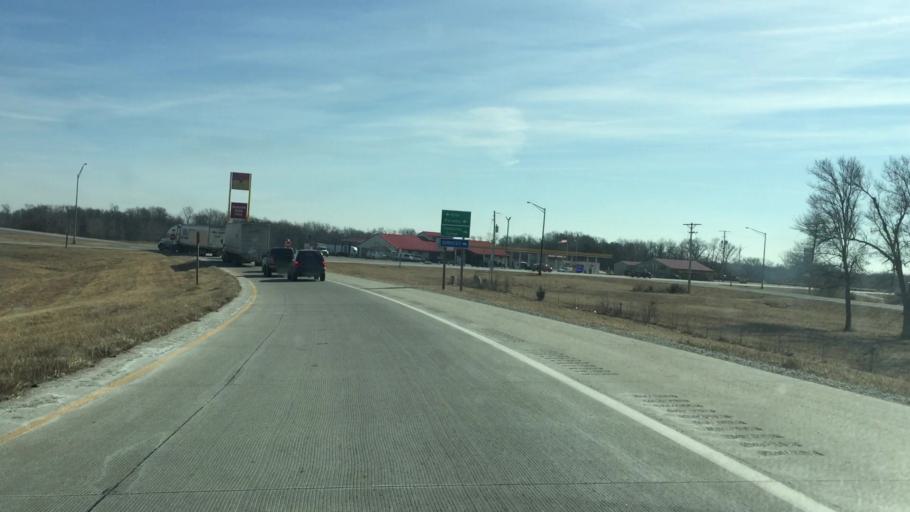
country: US
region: Kansas
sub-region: Labette County
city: Parsons
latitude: 37.3660
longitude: -95.2601
